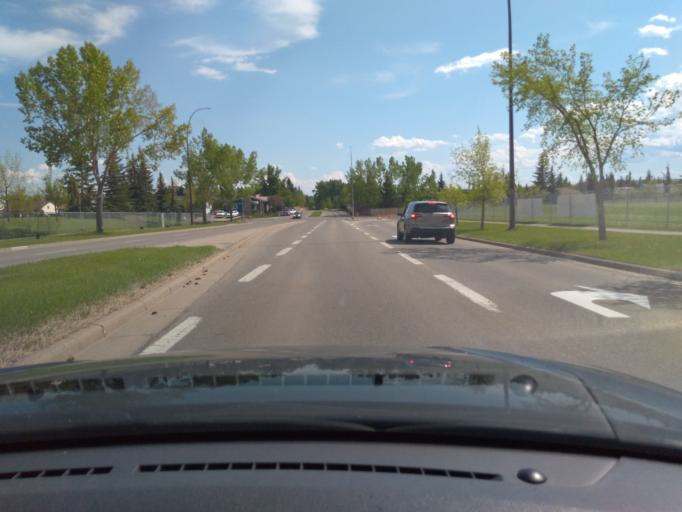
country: CA
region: Alberta
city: Calgary
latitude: 50.9370
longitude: -114.1181
